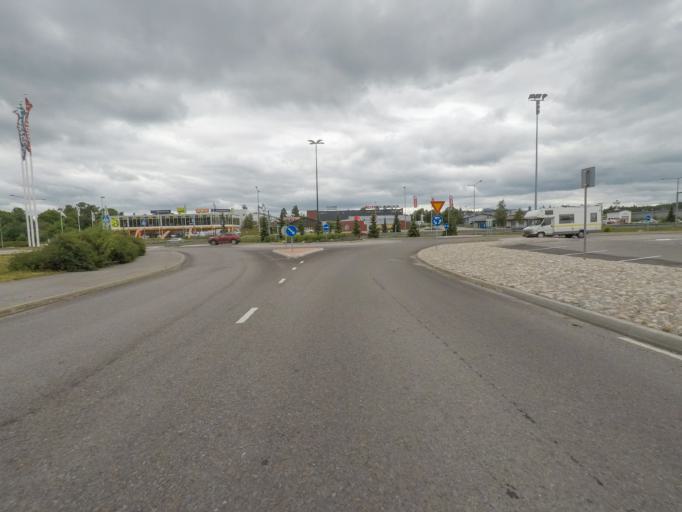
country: FI
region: Varsinais-Suomi
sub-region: Turku
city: Raisio
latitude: 60.4907
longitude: 22.1953
